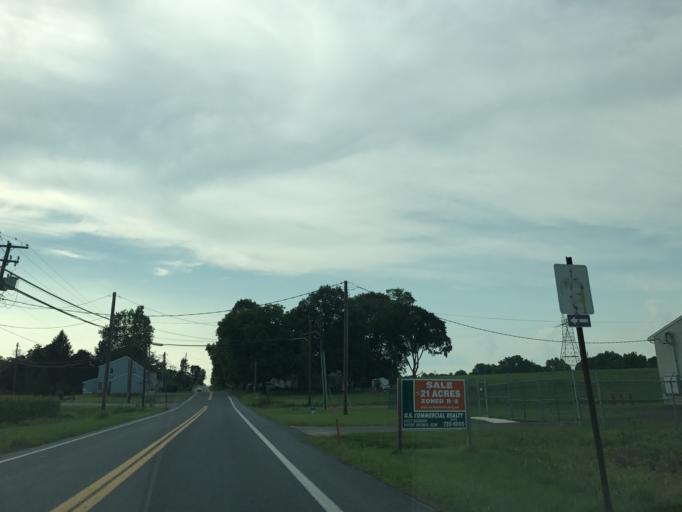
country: US
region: Pennsylvania
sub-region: Lancaster County
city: Rheems
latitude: 40.1209
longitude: -76.5439
